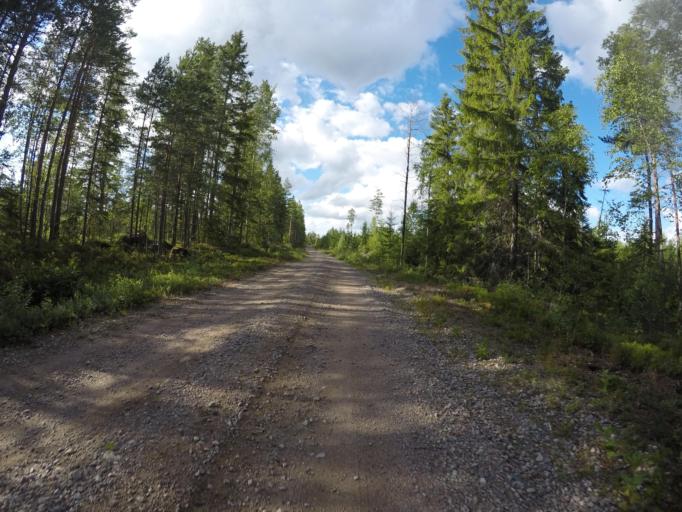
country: SE
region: OErebro
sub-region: Hallefors Kommun
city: Haellefors
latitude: 59.9469
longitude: 14.5642
